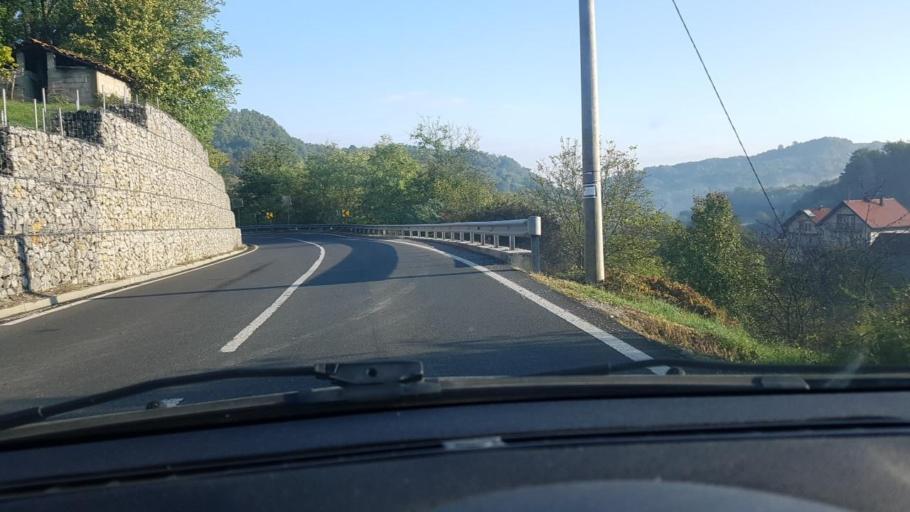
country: HR
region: Krapinsko-Zagorska
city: Marija Bistrica
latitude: 45.9782
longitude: 16.1057
